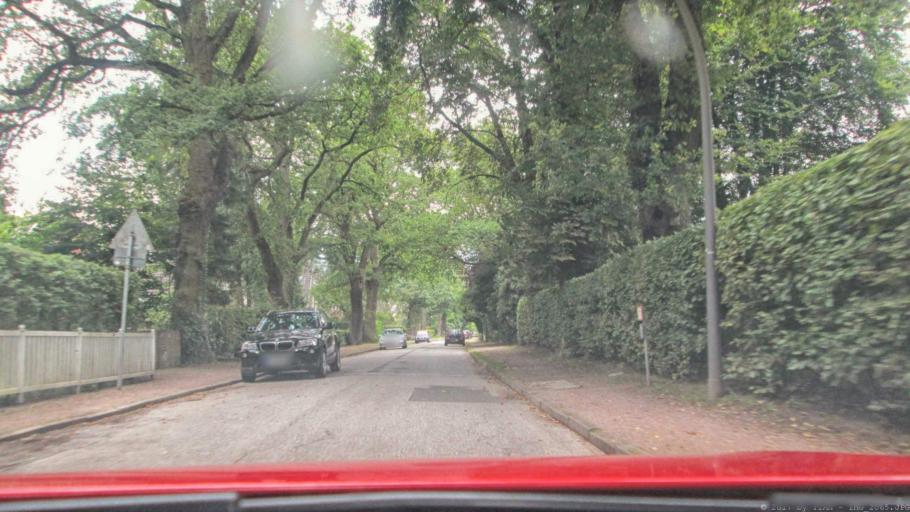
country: DE
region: Hamburg
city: Eidelstedt
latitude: 53.5624
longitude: 9.8529
